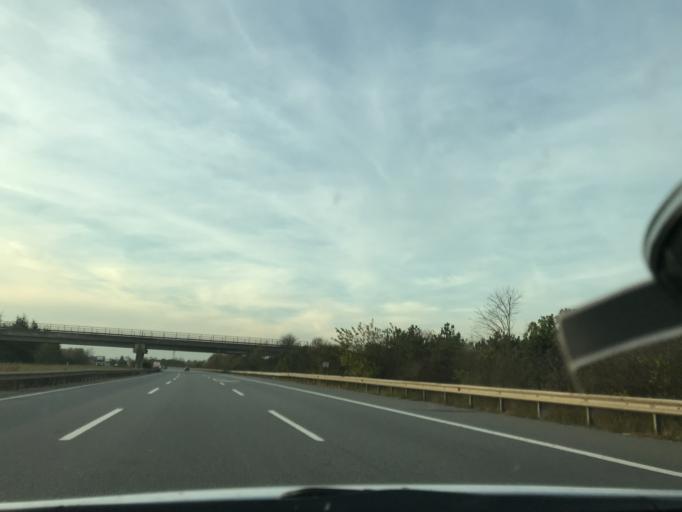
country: TR
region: Duzce
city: Cilimli
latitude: 40.8415
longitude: 31.0241
